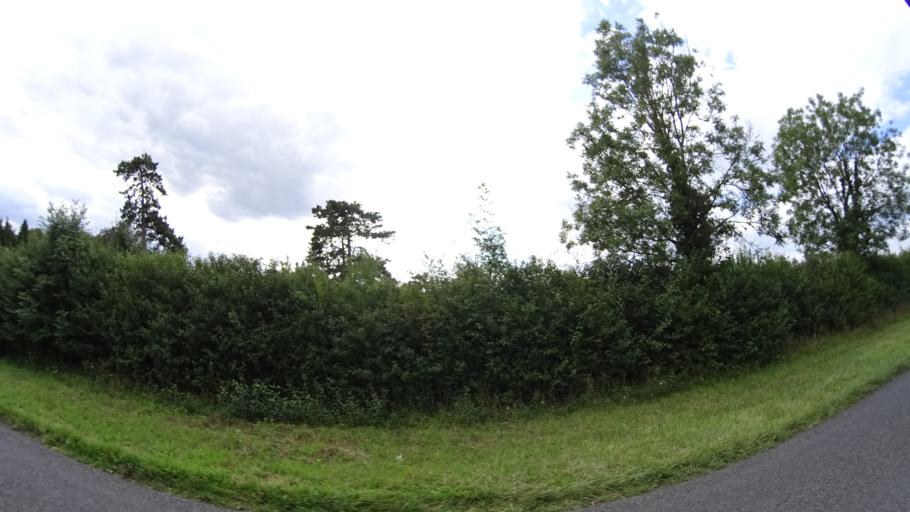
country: GB
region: England
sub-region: Wiltshire
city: Tidworth
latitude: 51.1805
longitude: -1.6492
